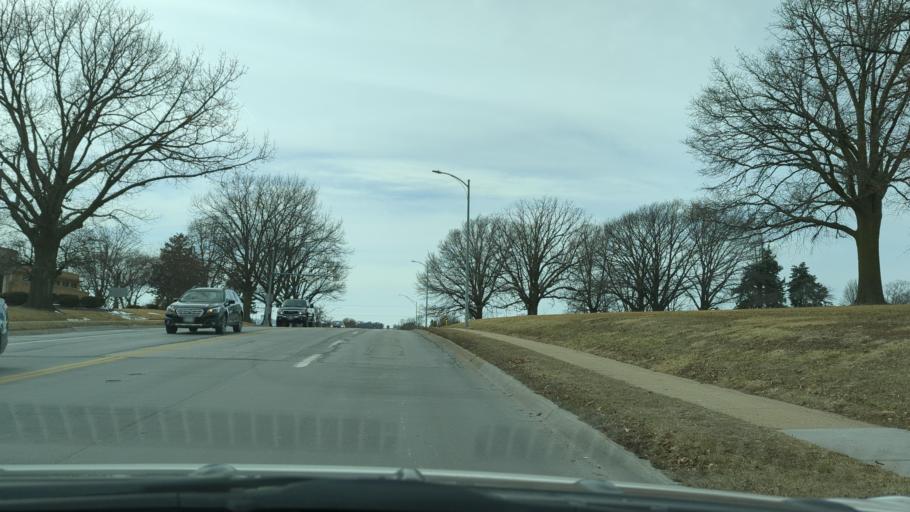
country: US
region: Nebraska
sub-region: Douglas County
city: Ralston
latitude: 41.2633
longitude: -96.0197
